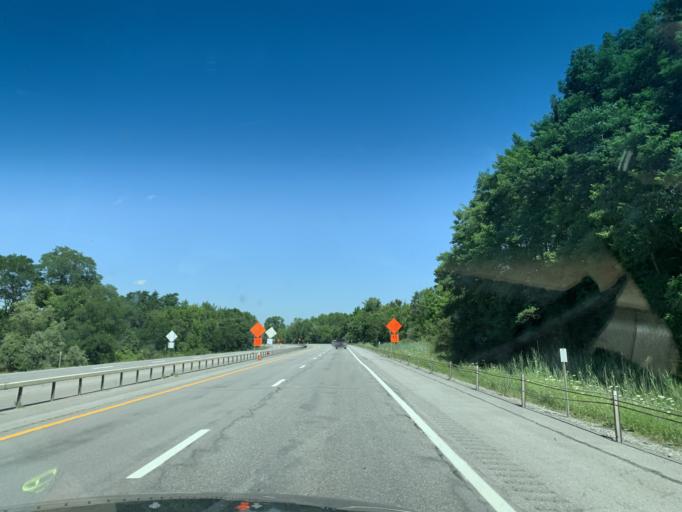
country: US
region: New York
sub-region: Oneida County
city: Chadwicks
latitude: 43.0132
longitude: -75.2548
